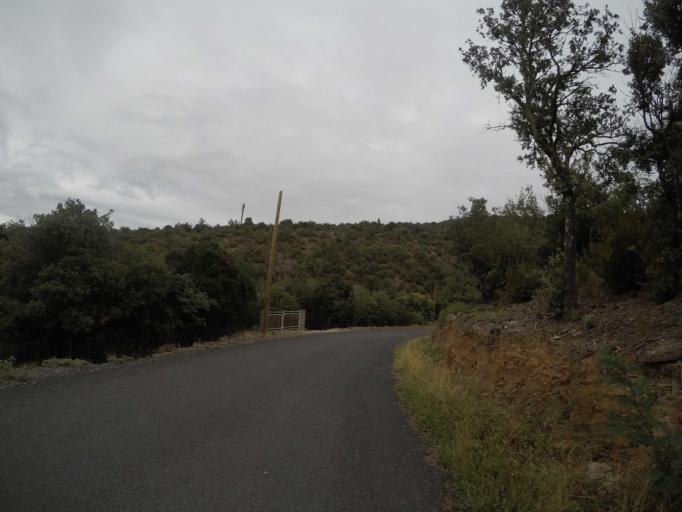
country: FR
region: Languedoc-Roussillon
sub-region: Departement des Pyrenees-Orientales
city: Ille-sur-Tet
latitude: 42.6160
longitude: 2.6154
